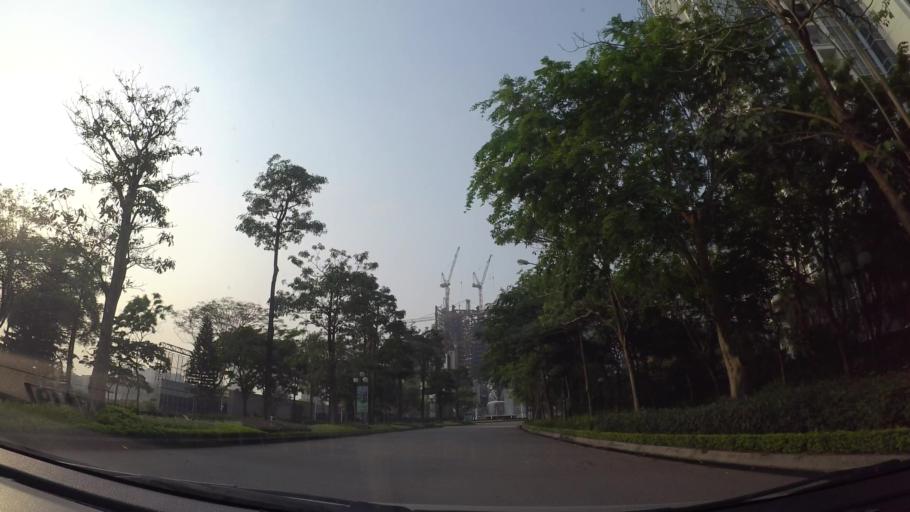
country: VN
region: Ha Noi
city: Tay Ho
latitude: 21.0800
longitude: 105.7912
